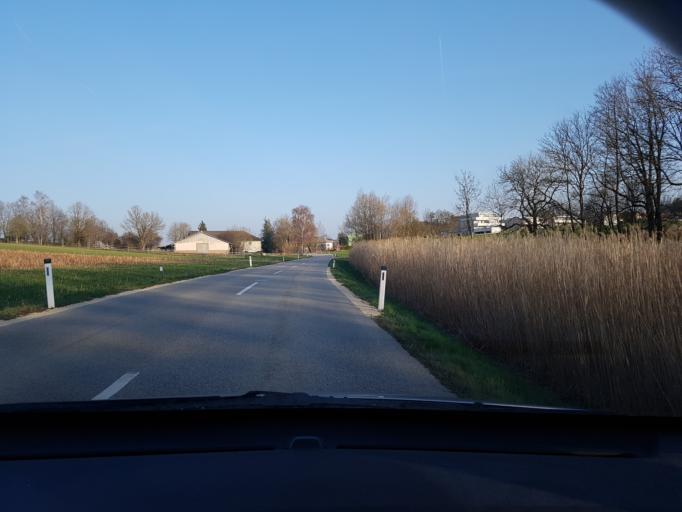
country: AT
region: Upper Austria
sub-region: Politischer Bezirk Linz-Land
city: Ansfelden
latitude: 48.1535
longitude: 14.2628
